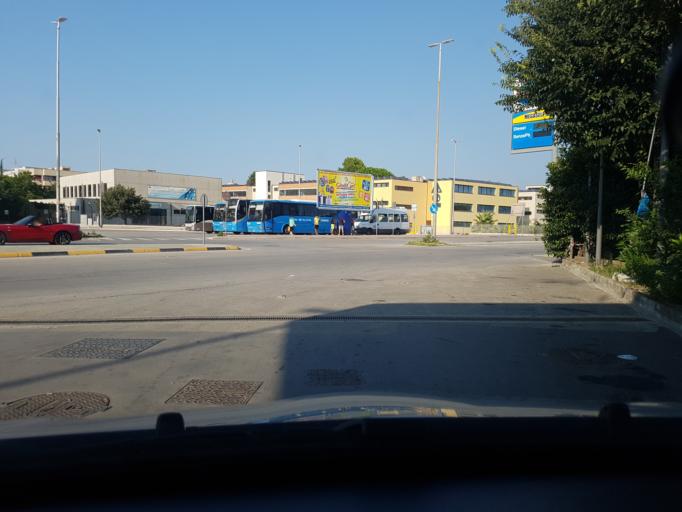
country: IT
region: Apulia
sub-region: Provincia di Foggia
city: Cerignola
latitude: 41.2601
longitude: 15.9078
